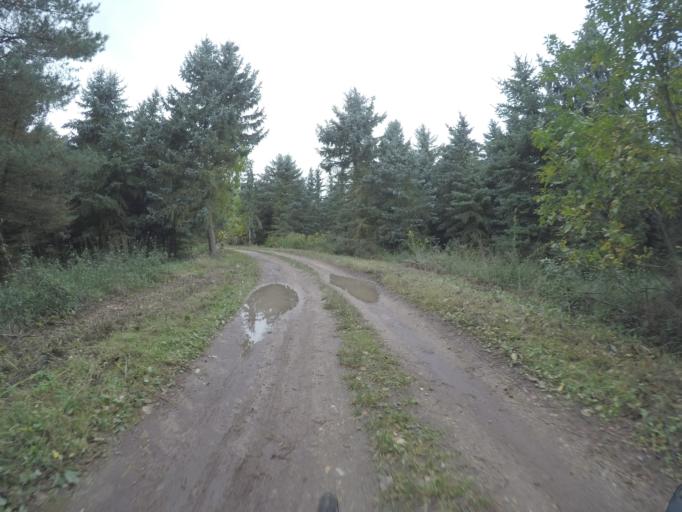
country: DE
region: Berlin
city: Buch
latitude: 52.6552
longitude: 13.4915
